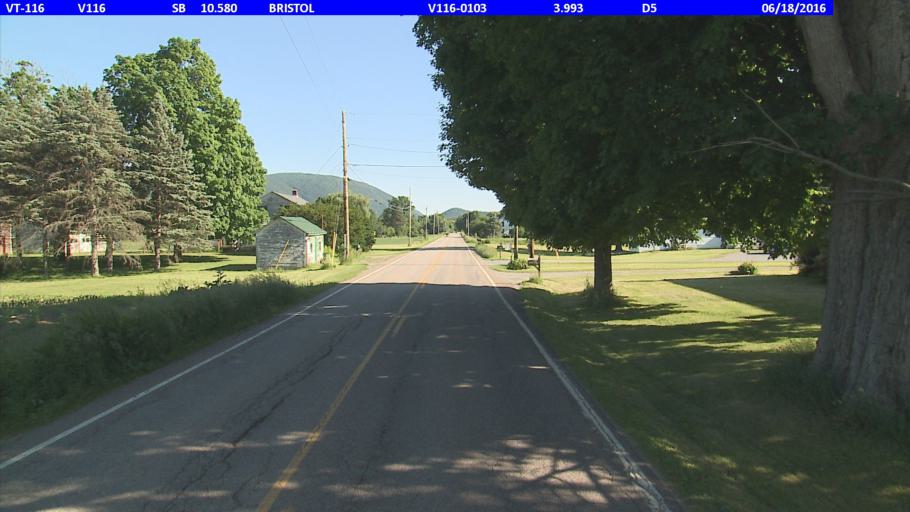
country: US
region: Vermont
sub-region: Addison County
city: Bristol
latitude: 44.1081
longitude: -73.0970
